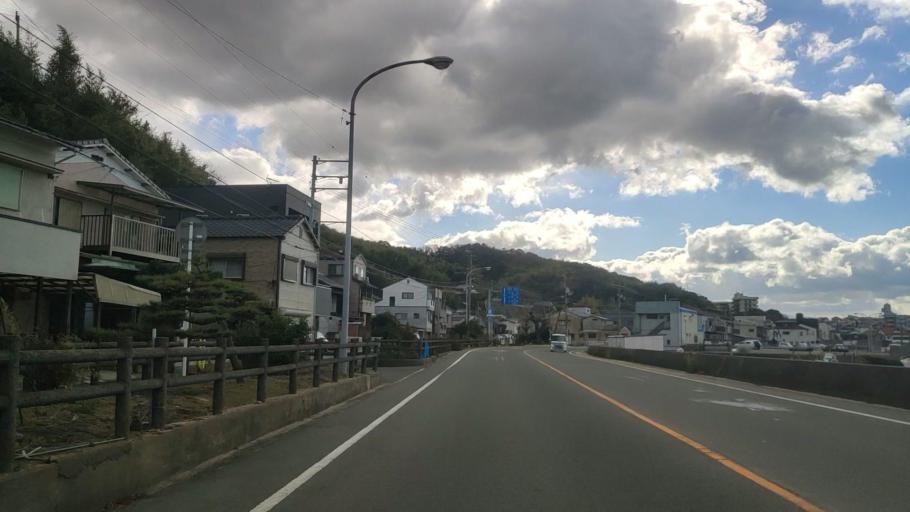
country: JP
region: Ehime
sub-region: Shikoku-chuo Shi
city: Matsuyama
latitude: 33.8854
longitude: 132.7010
